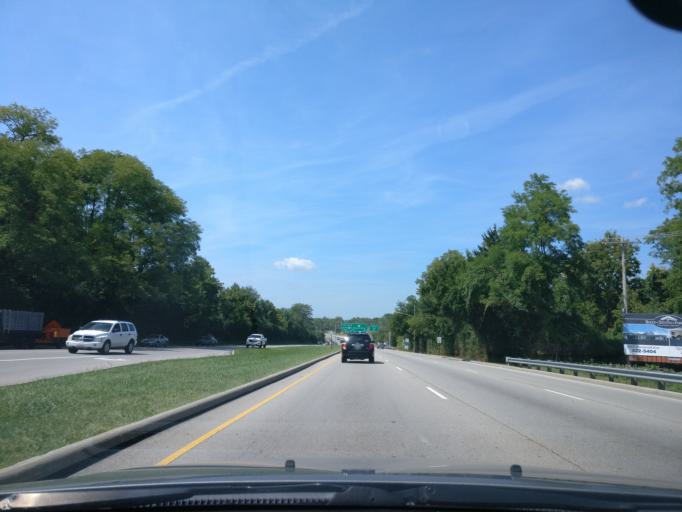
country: US
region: Ohio
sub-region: Butler County
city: Mayfield
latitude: 39.4969
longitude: -84.3375
